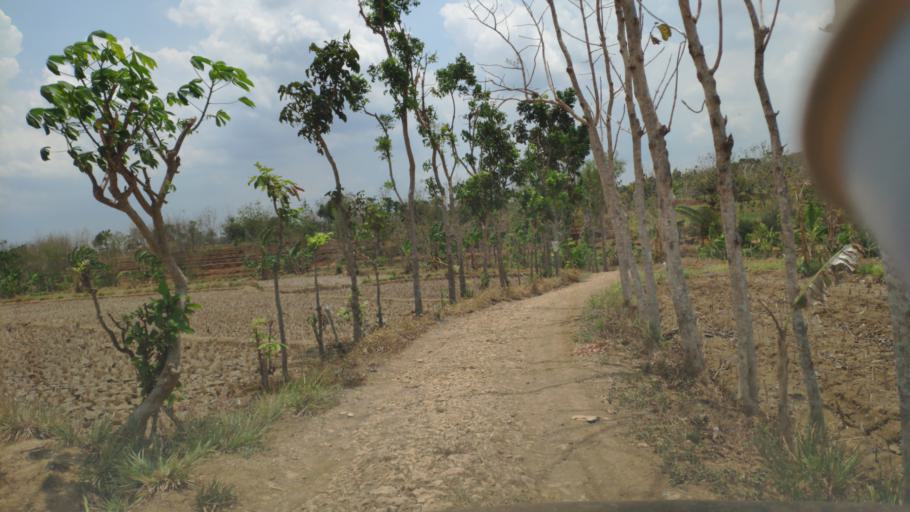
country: ID
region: Central Java
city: Ngapus
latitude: -6.9535
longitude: 111.1870
